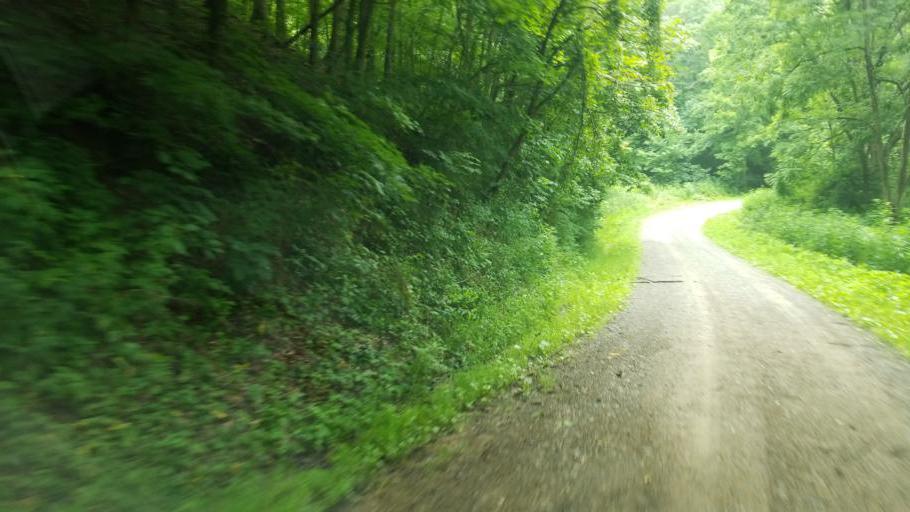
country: US
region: Ohio
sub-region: Columbiana County
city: Salineville
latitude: 40.5607
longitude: -80.8070
